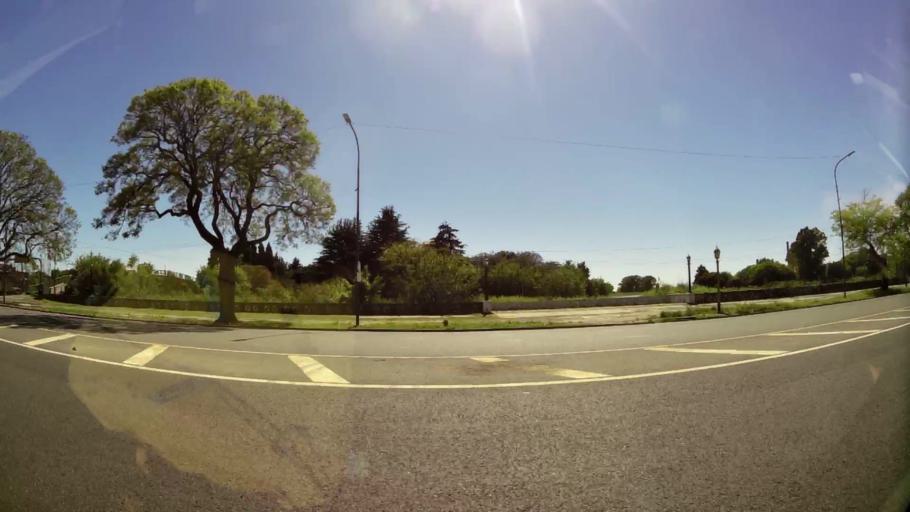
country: AR
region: Buenos Aires F.D.
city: Buenos Aires
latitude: -34.6210
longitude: -58.3549
